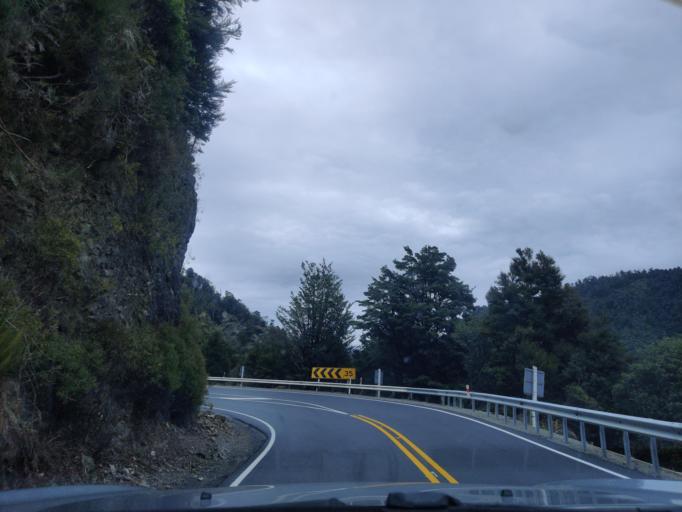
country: NZ
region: Tasman
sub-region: Tasman District
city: Wakefield
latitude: -41.6963
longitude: 172.6166
